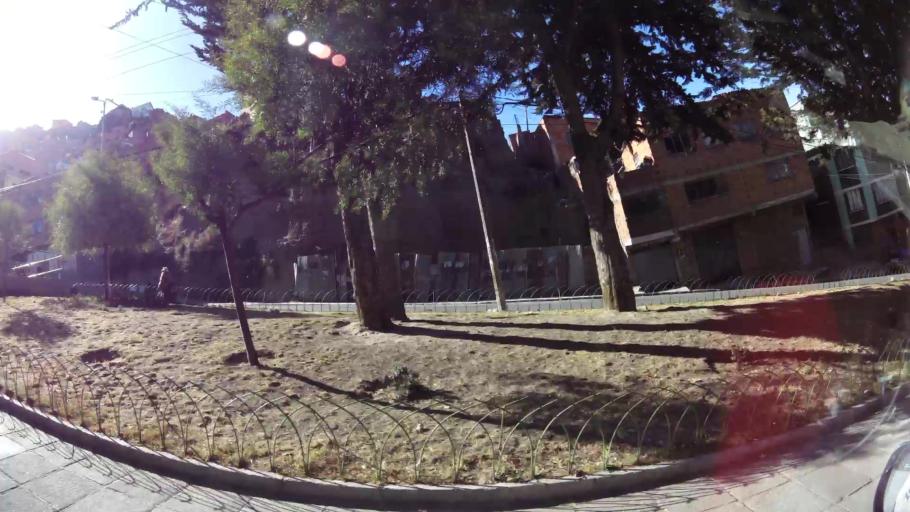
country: BO
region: La Paz
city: La Paz
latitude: -16.5105
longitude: -68.1462
